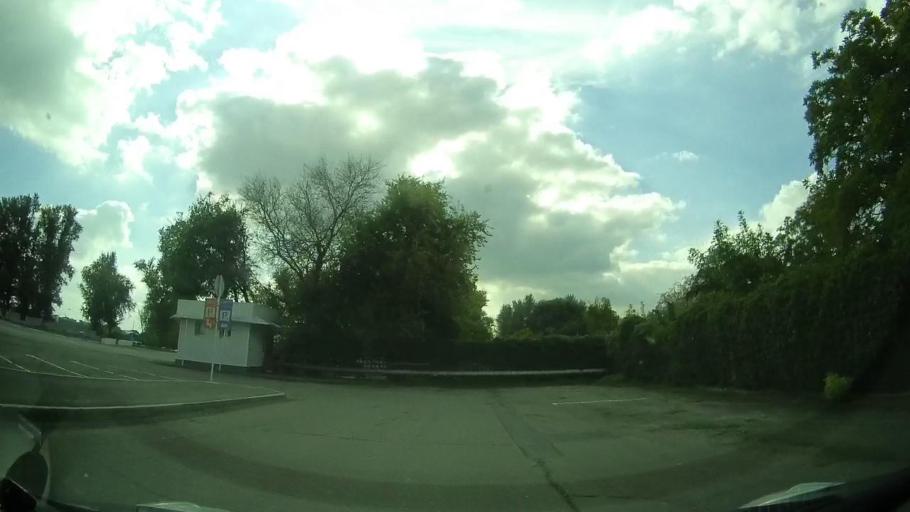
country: RU
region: Rostov
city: Imeni Chkalova
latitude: 47.2552
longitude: 39.8020
